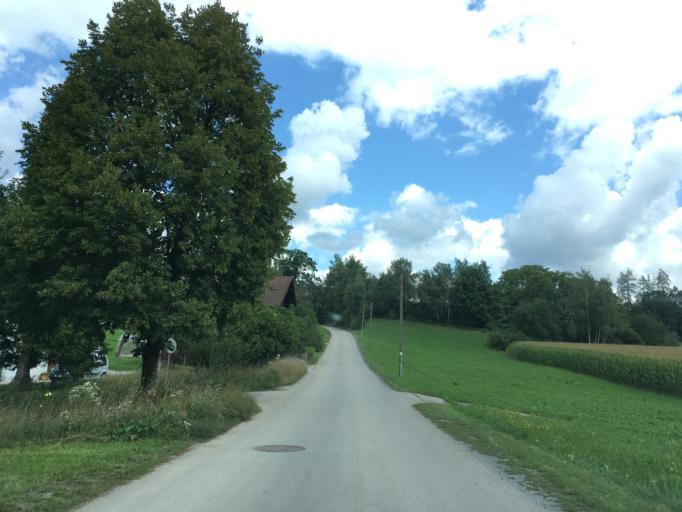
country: DE
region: Bavaria
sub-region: Upper Bavaria
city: Schnaitsee
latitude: 48.0690
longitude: 12.3329
